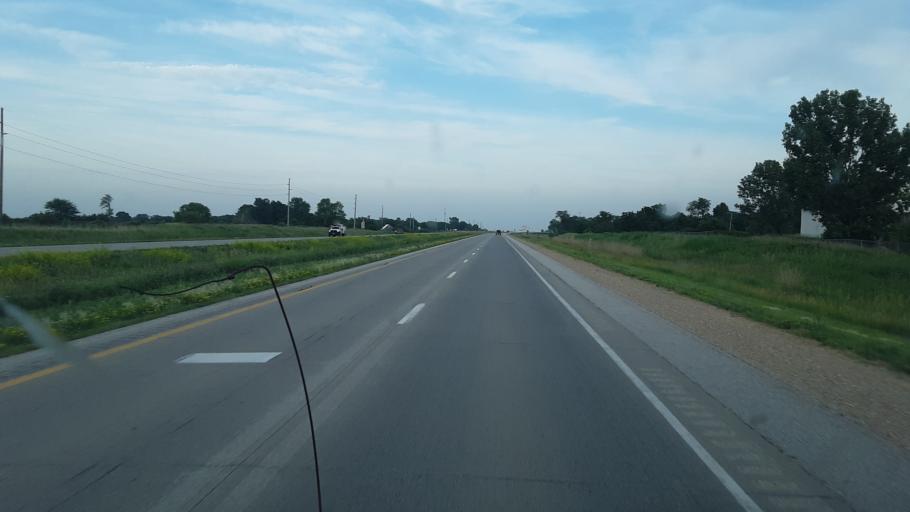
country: US
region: Iowa
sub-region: Tama County
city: Toledo
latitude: 41.9970
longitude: -92.6393
